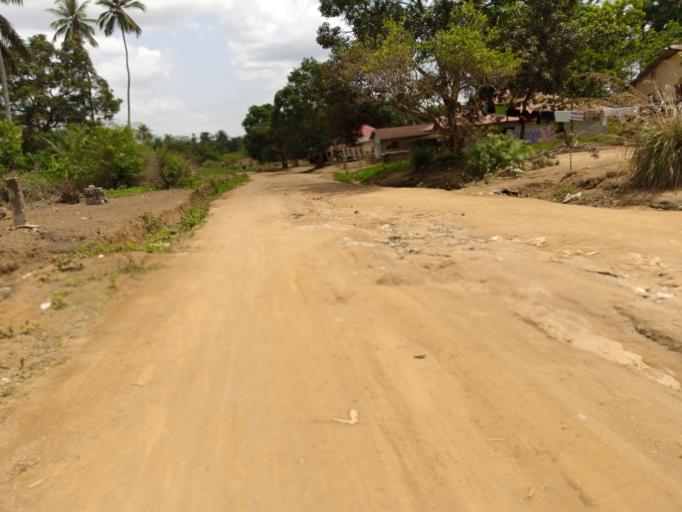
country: SL
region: Western Area
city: Waterloo
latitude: 8.3299
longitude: -13.0158
